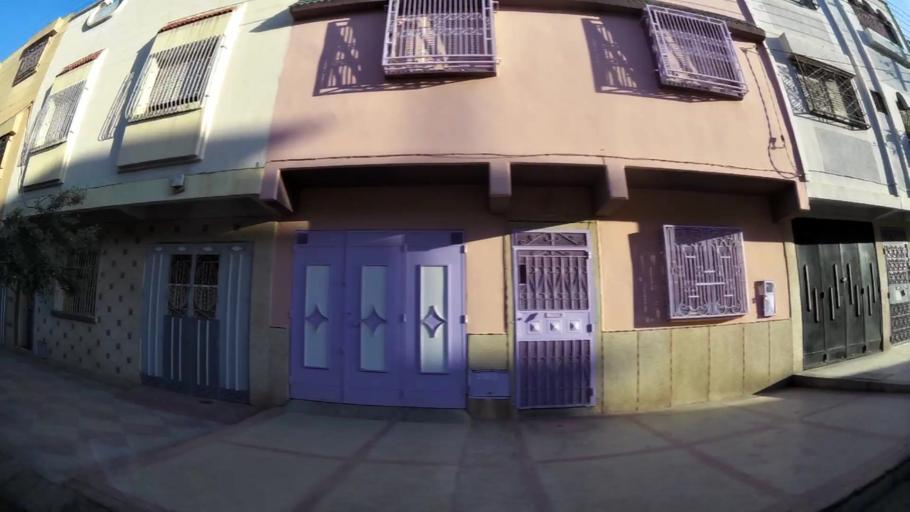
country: MA
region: Oriental
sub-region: Oujda-Angad
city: Oujda
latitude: 34.7009
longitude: -1.9140
